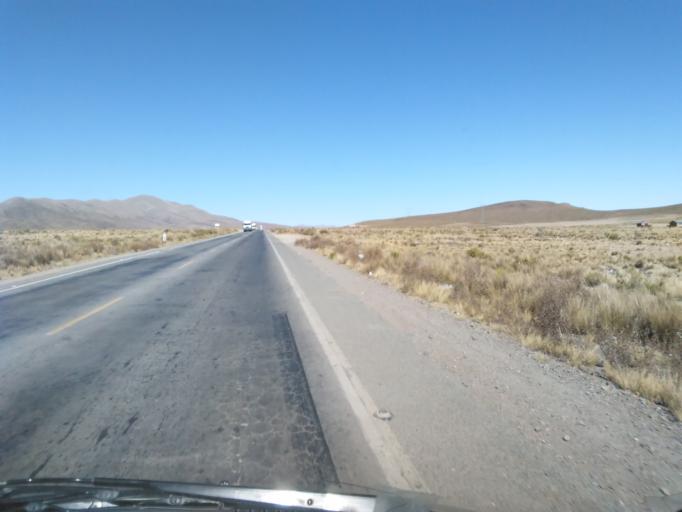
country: BO
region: Oruro
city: Machacamarca
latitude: -18.0398
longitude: -67.0159
